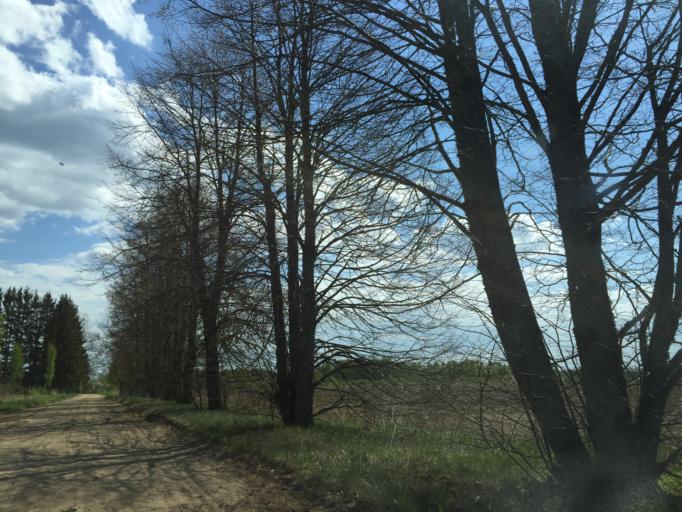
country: LV
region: Saulkrastu
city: Saulkrasti
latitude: 57.3610
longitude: 24.4922
